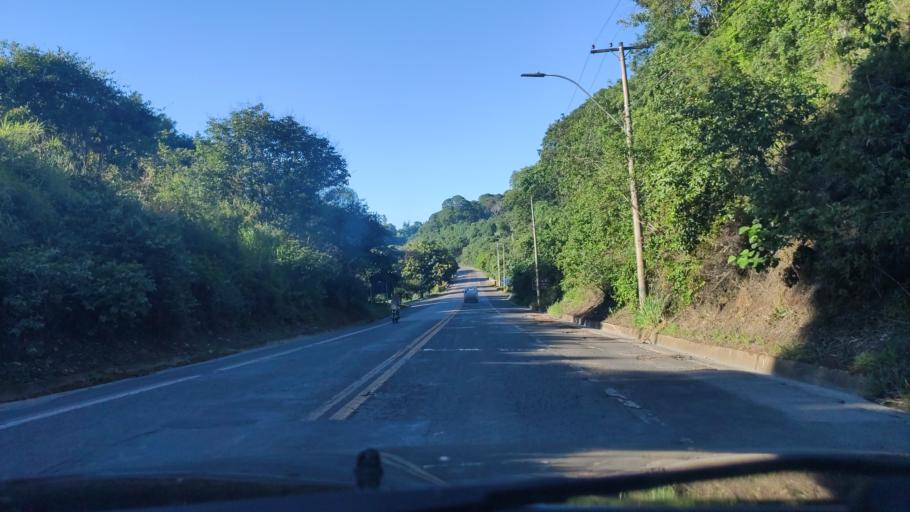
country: BR
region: Sao Paulo
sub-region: Socorro
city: Socorro
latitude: -22.5947
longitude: -46.5162
